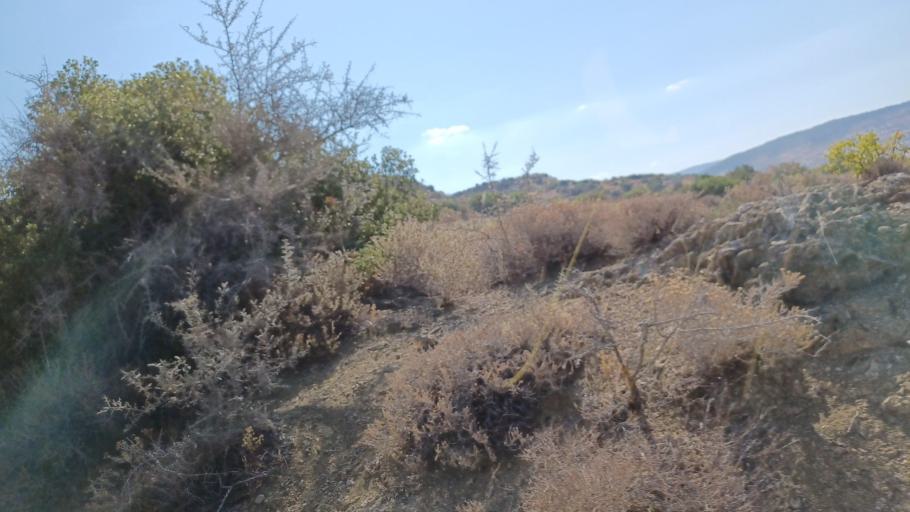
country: CY
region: Pafos
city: Polis
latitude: 34.9667
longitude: 32.4960
